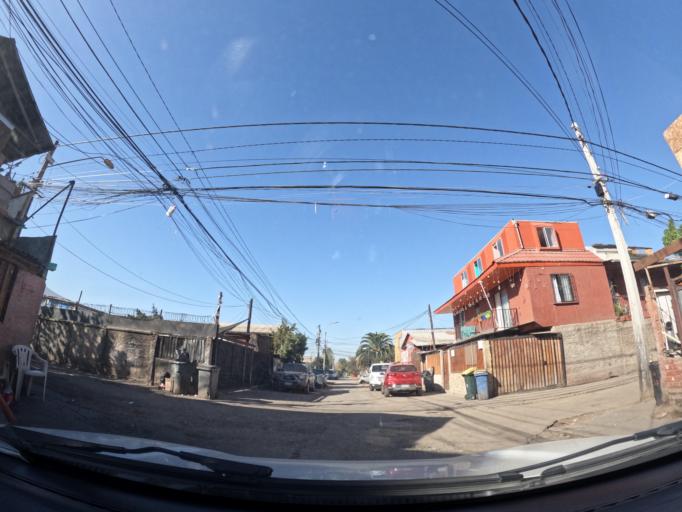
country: CL
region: Santiago Metropolitan
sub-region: Provincia de Santiago
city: Villa Presidente Frei, Nunoa, Santiago, Chile
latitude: -33.4631
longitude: -70.5628
